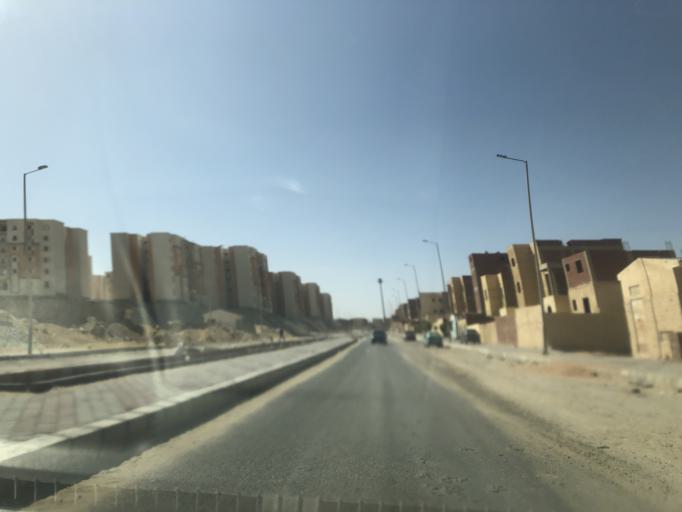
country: EG
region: Al Jizah
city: Madinat Sittah Uktubar
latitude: 29.9336
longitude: 30.9822
